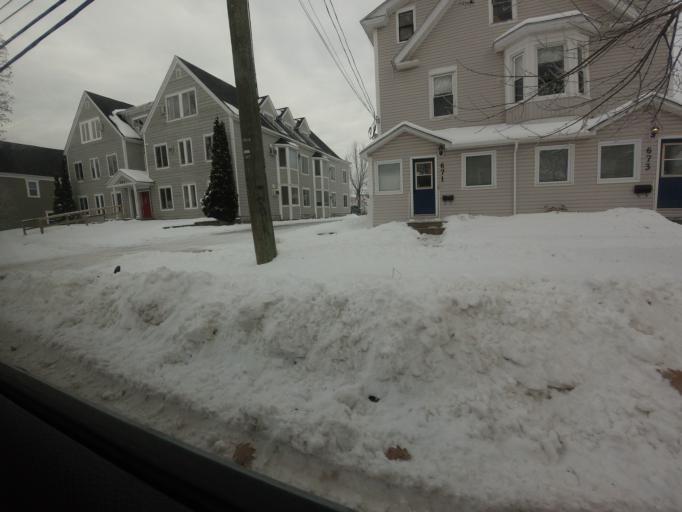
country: CA
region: New Brunswick
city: Fredericton
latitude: 45.9567
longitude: -66.6403
